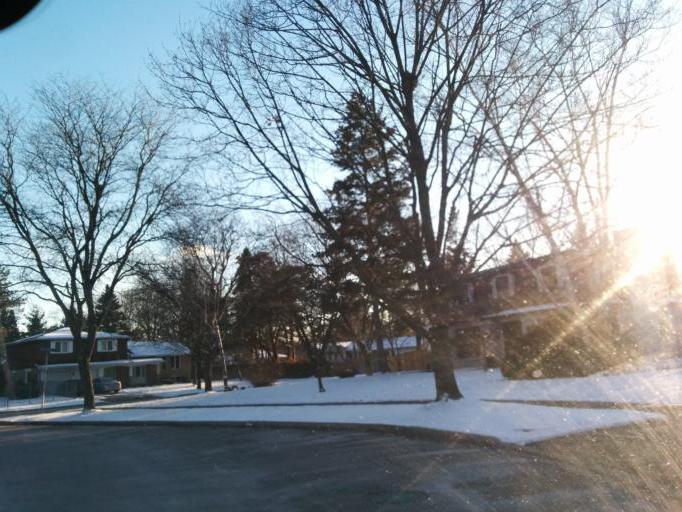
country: CA
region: Ontario
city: Mississauga
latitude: 43.5448
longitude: -79.6126
